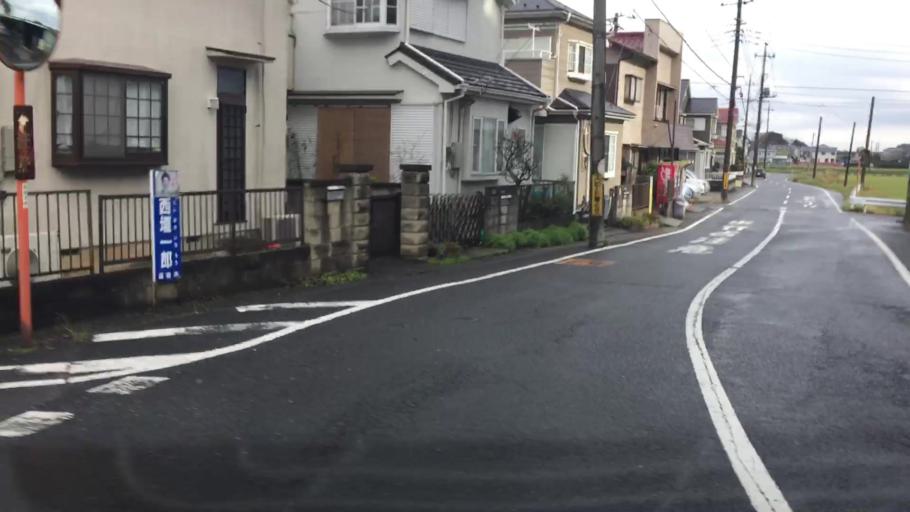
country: JP
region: Ibaraki
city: Toride
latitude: 35.8644
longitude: 140.1157
